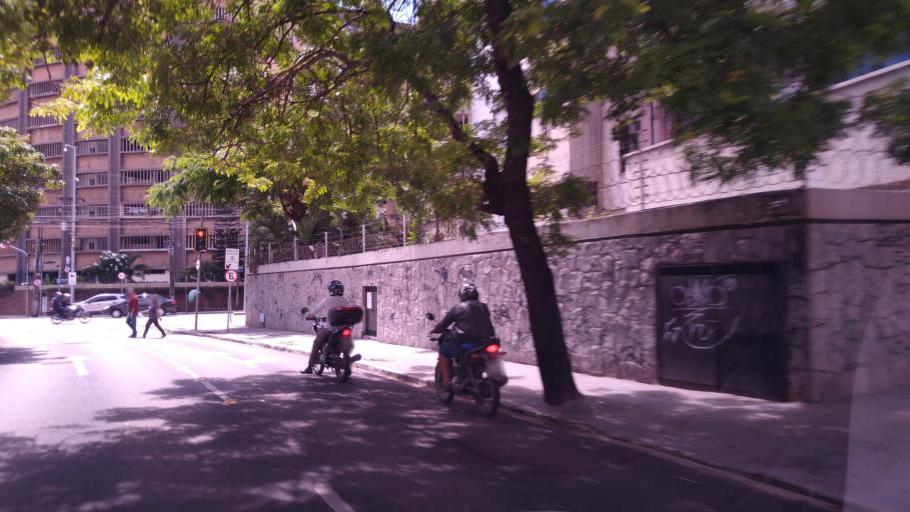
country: BR
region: Ceara
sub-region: Fortaleza
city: Fortaleza
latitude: -3.7293
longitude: -38.4907
